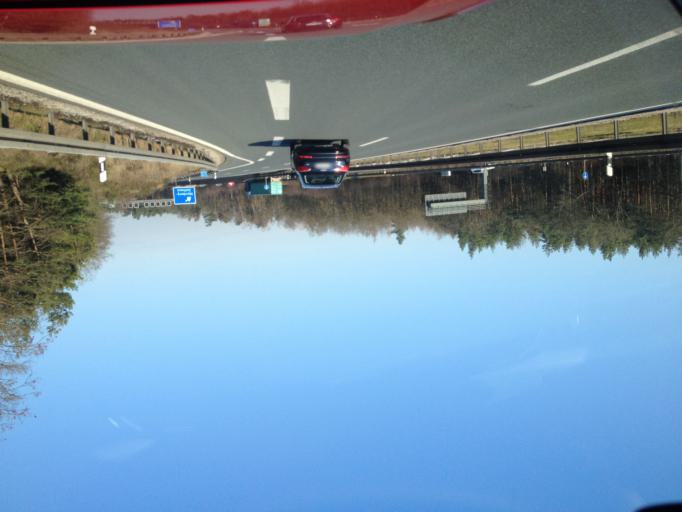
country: DE
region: Bavaria
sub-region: Regierungsbezirk Mittelfranken
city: Wendelstein
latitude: 49.3804
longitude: 11.1337
